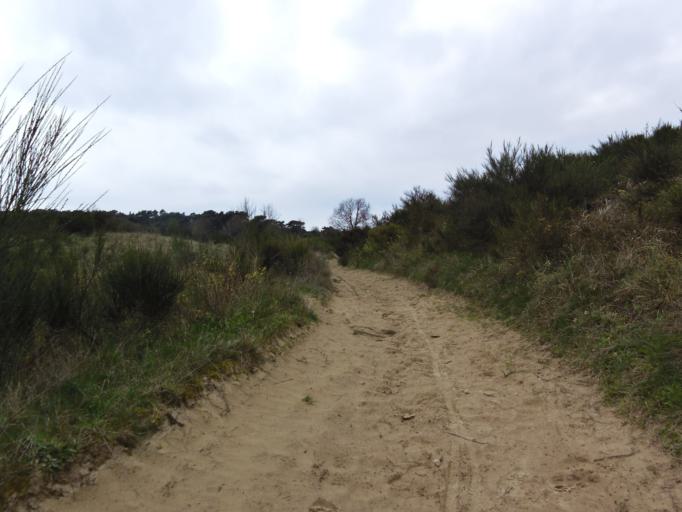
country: DE
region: Mecklenburg-Vorpommern
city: Hiddensee
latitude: 54.5942
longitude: 13.1223
